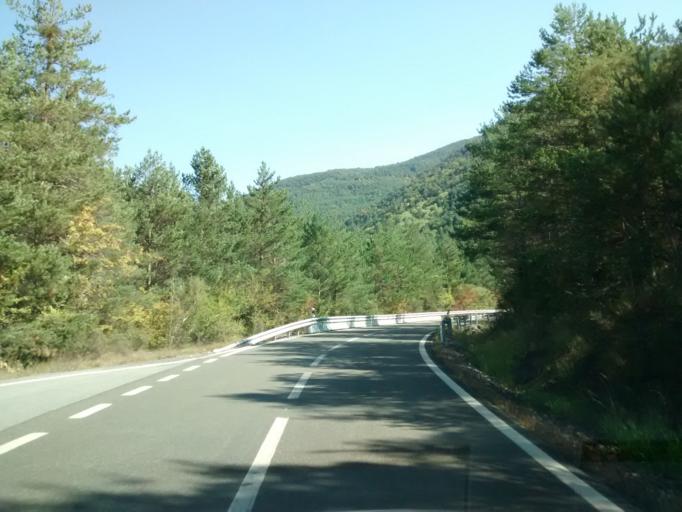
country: ES
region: Aragon
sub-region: Provincia de Huesca
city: Fiscal
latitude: 42.5476
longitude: -0.1273
